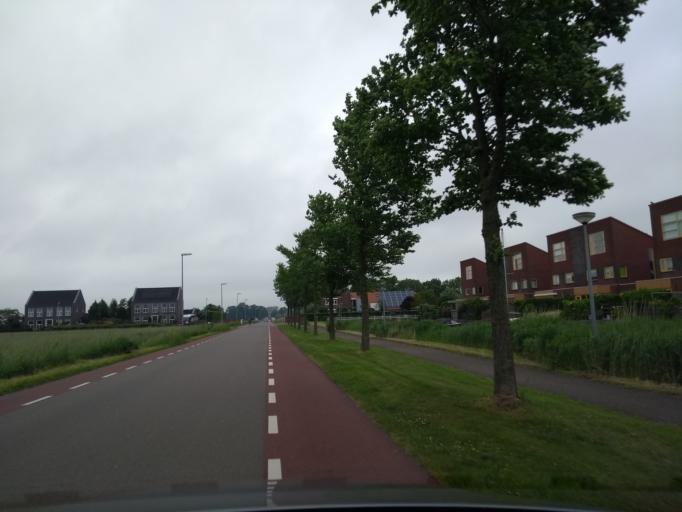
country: NL
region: Groningen
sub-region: Gemeente Groningen
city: Korrewegwijk
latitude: 53.2449
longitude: 6.5188
